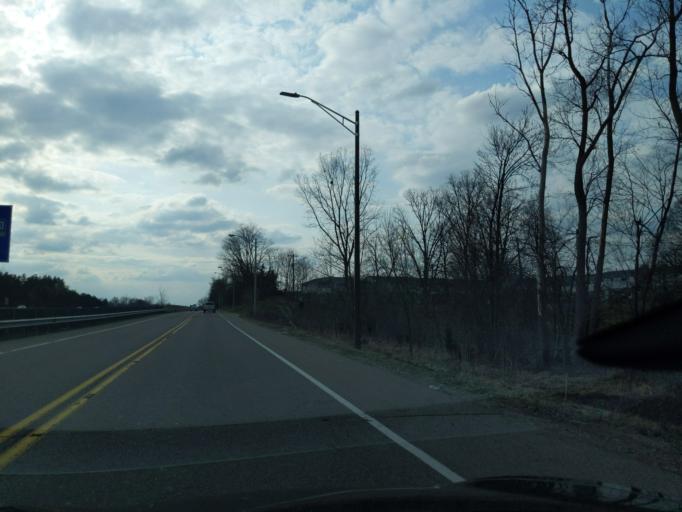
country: US
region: Michigan
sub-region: Ingham County
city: Holt
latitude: 42.6627
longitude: -84.5730
